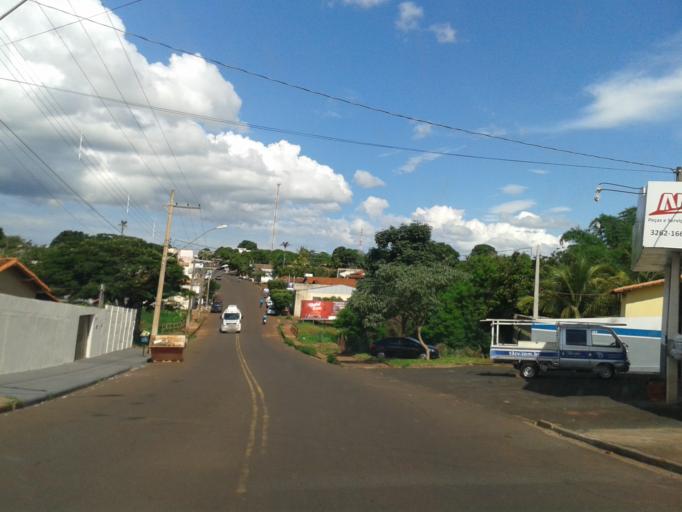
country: BR
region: Minas Gerais
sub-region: Ituiutaba
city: Ituiutaba
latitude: -18.9853
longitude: -49.4752
